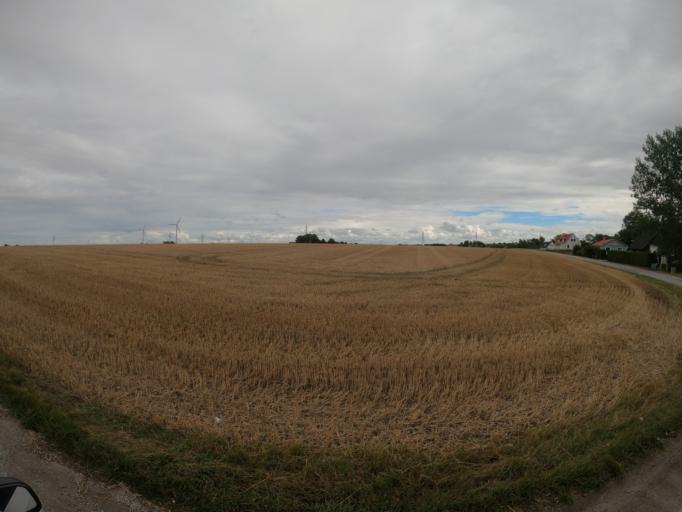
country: SE
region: Skane
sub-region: Kavlinge Kommun
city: Kaevlinge
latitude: 55.7463
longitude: 13.1354
